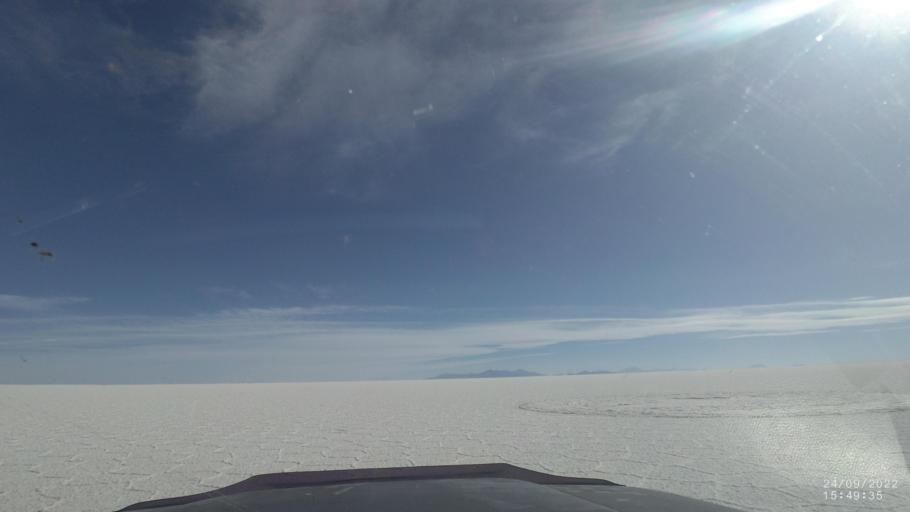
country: BO
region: Potosi
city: Colchani
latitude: -20.3018
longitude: -67.2424
